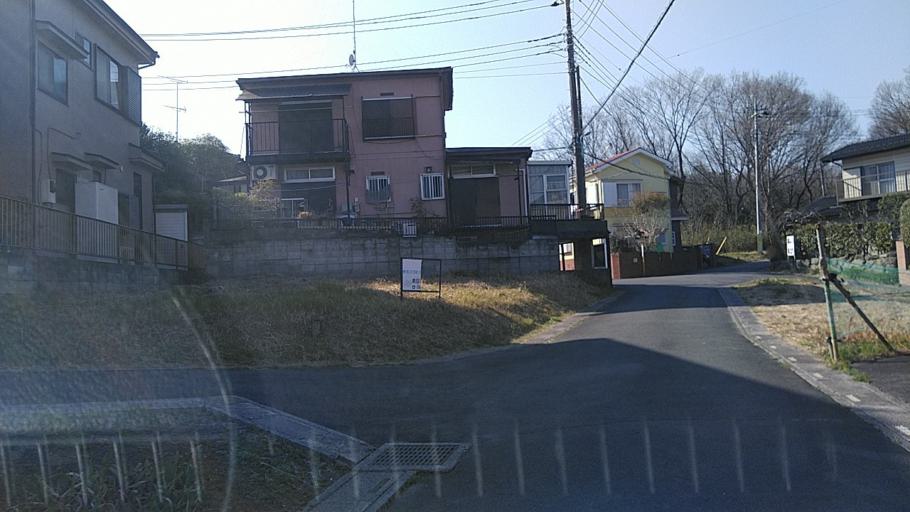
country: JP
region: Saitama
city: Fukiage-fujimi
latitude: 36.0773
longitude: 139.4013
